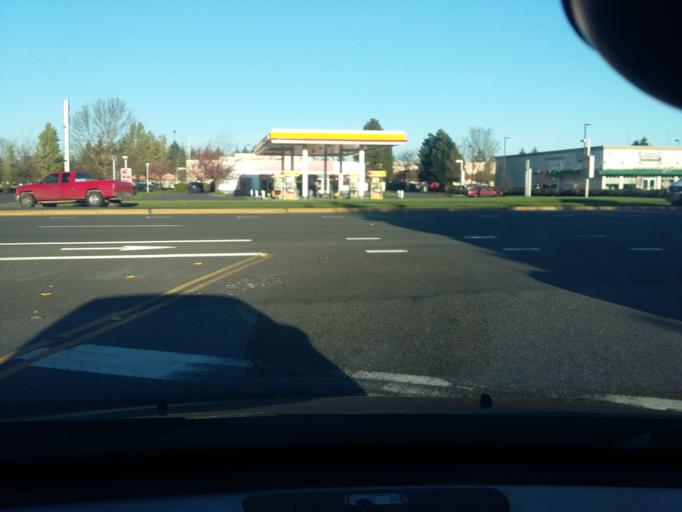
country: US
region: Washington
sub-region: Clark County
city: Barberton
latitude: 45.6842
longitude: -122.6026
